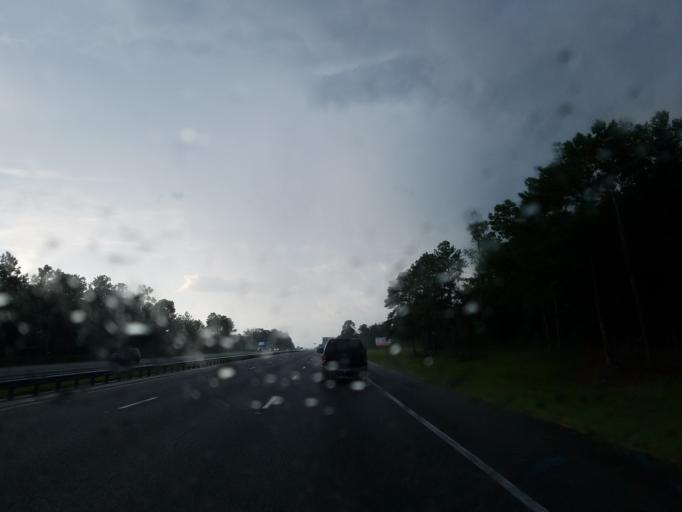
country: US
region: Georgia
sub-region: Lowndes County
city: Valdosta
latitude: 30.7296
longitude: -83.2612
